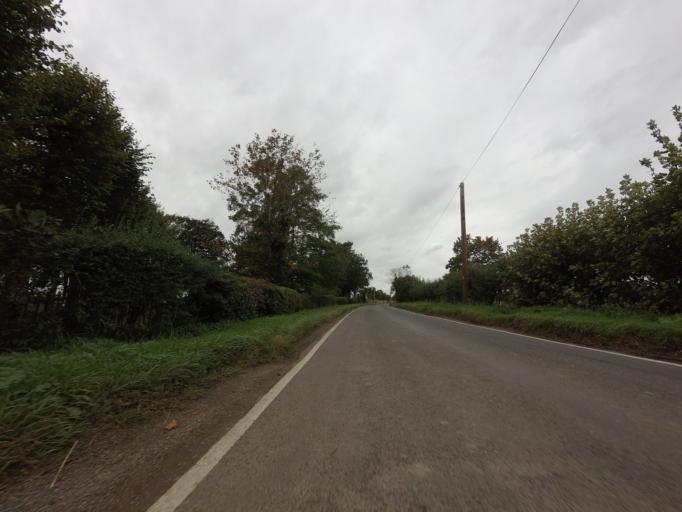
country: GB
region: England
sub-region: Cambridgeshire
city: Harston
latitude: 52.0989
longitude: 0.0622
